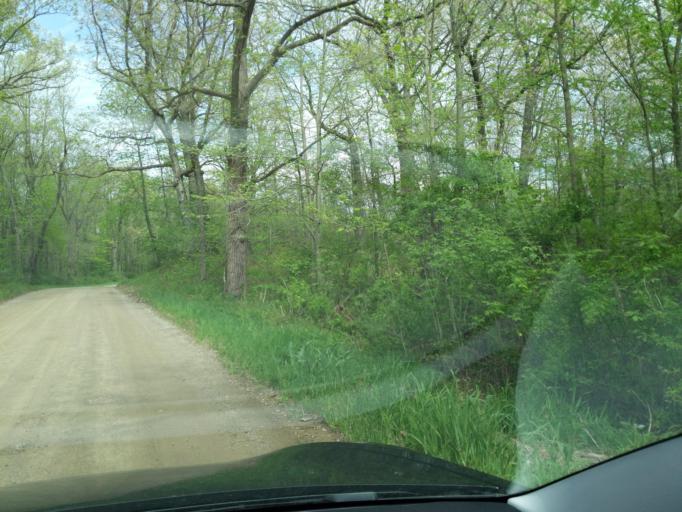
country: US
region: Michigan
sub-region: Washtenaw County
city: Chelsea
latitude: 42.4093
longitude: -84.0694
